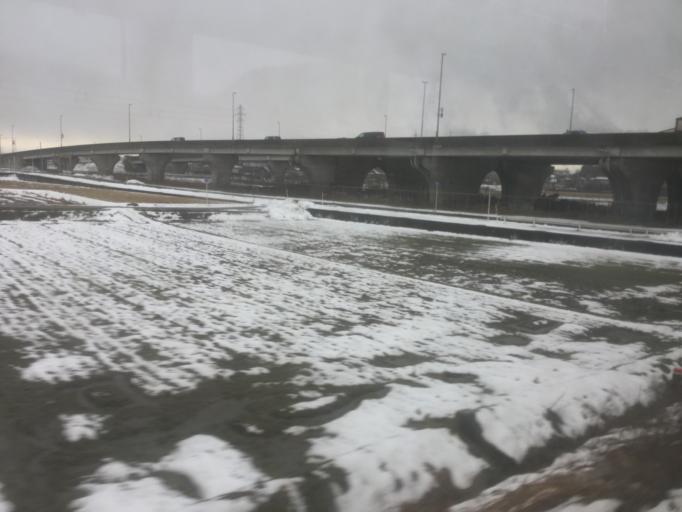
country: JP
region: Toyama
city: Takaoka
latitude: 36.7190
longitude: 137.0085
